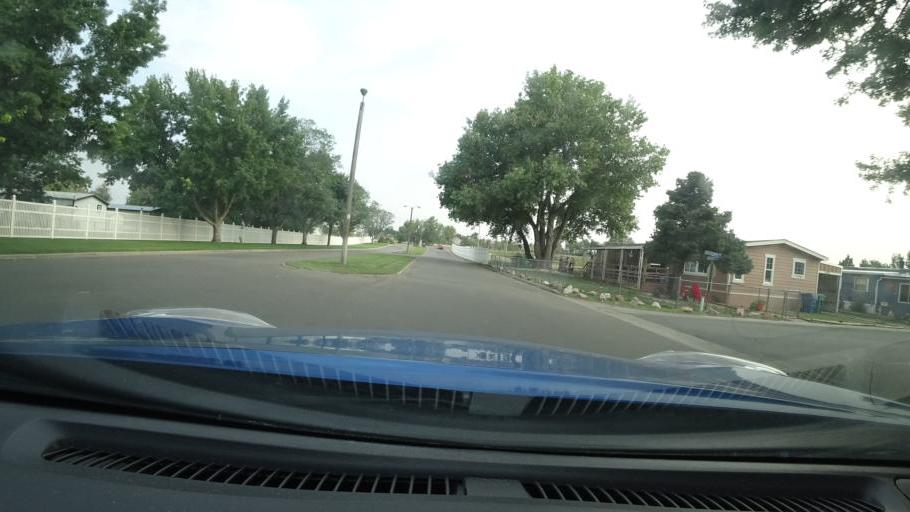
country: US
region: Colorado
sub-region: Adams County
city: Aurora
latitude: 39.7416
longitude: -104.7869
